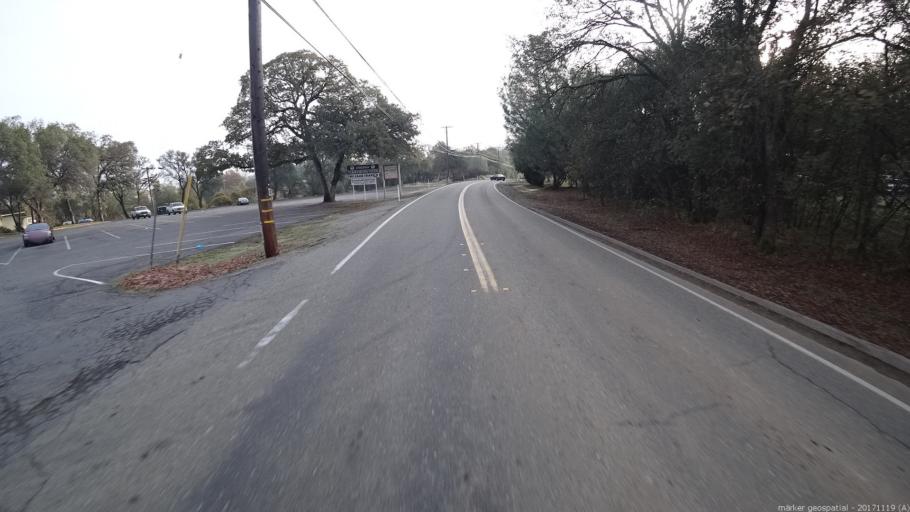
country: US
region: California
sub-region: Shasta County
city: Anderson
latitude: 40.4817
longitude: -122.3021
